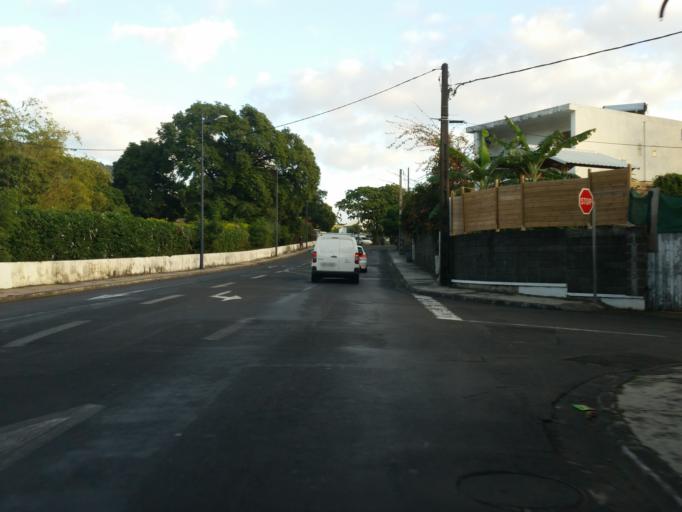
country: RE
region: Reunion
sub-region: Reunion
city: Saint-Denis
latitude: -20.8928
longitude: 55.4557
